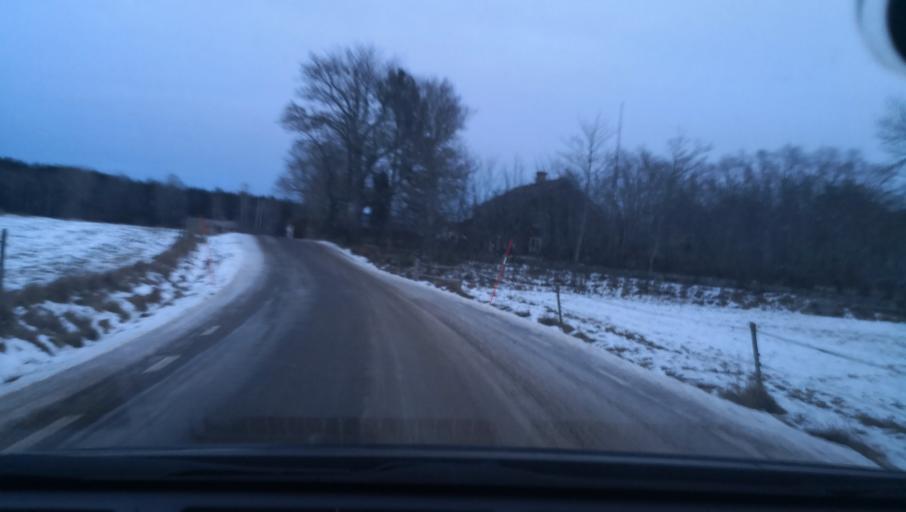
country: SE
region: Dalarna
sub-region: Avesta Kommun
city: Horndal
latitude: 60.1996
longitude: 16.4958
